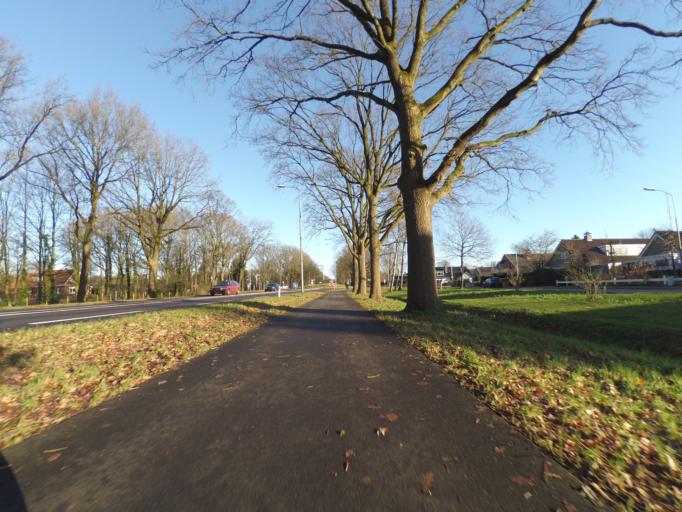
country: NL
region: Gelderland
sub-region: Gemeente Putten
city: Putten
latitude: 52.2630
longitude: 5.6022
